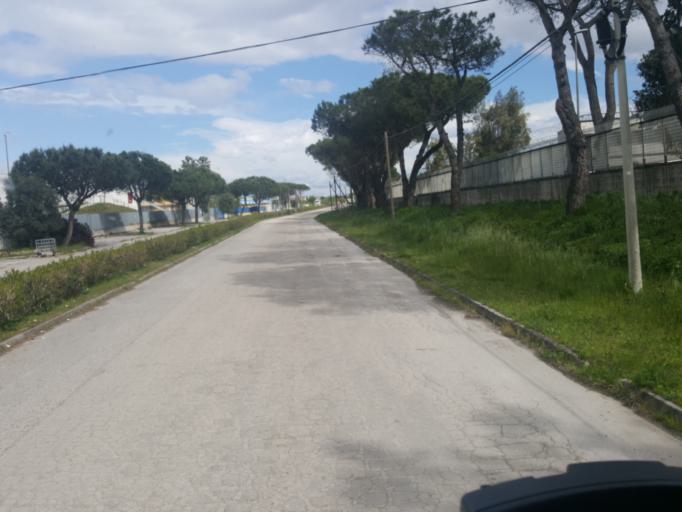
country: IT
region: Campania
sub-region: Provincia di Napoli
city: Torretta-Scalzapecora
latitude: 40.9345
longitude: 14.1176
